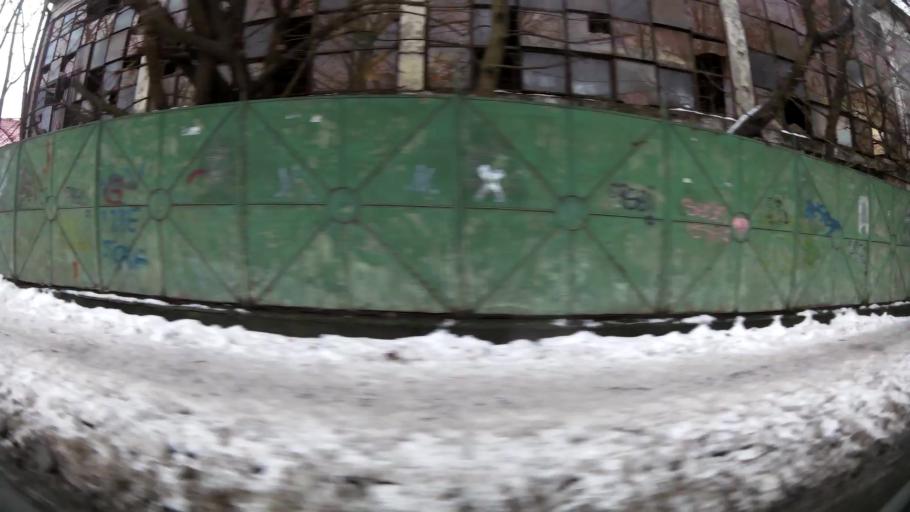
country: RO
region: Ilfov
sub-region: Comuna Pantelimon
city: Pantelimon
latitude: 44.4359
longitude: 26.1923
